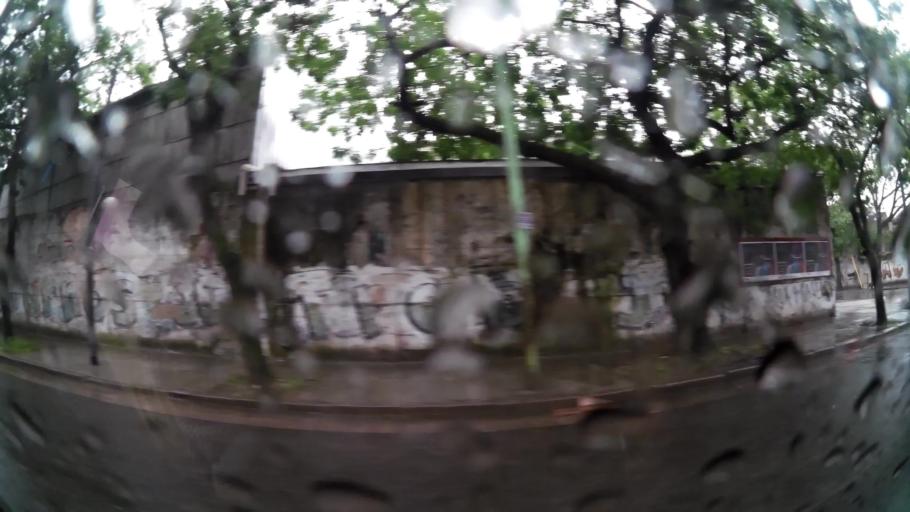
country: AR
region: Buenos Aires
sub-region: Partido de Avellaneda
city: Avellaneda
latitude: -34.6420
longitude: -58.3953
